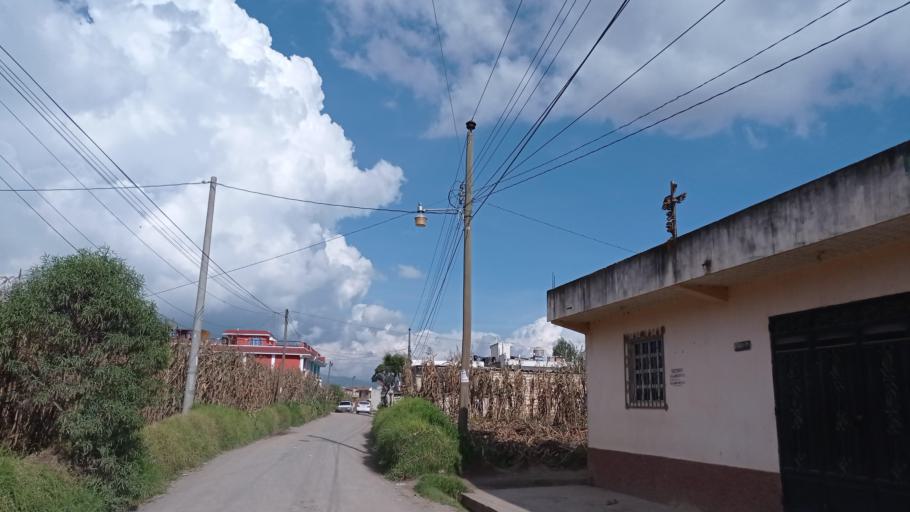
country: GT
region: Quetzaltenango
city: Olintepeque
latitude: 14.8695
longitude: -91.5014
